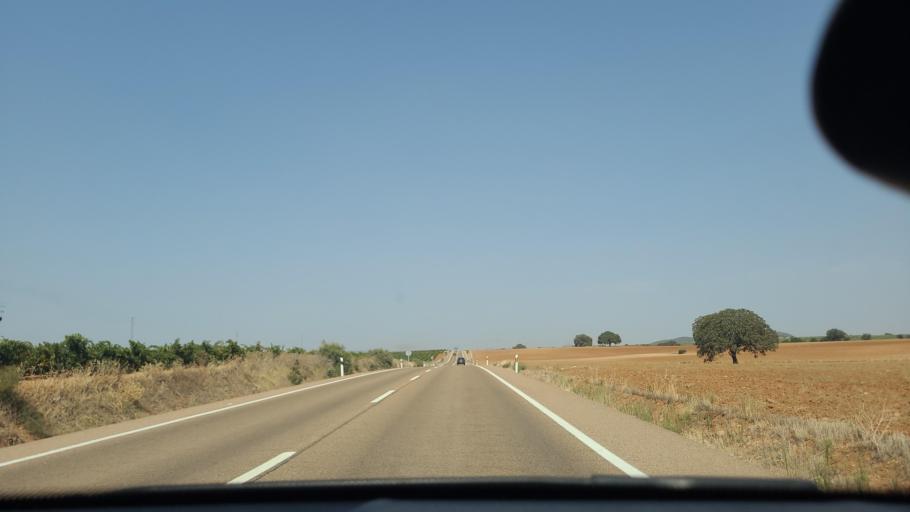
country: ES
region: Extremadura
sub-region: Provincia de Badajoz
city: Usagre
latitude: 38.3738
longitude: -6.2561
